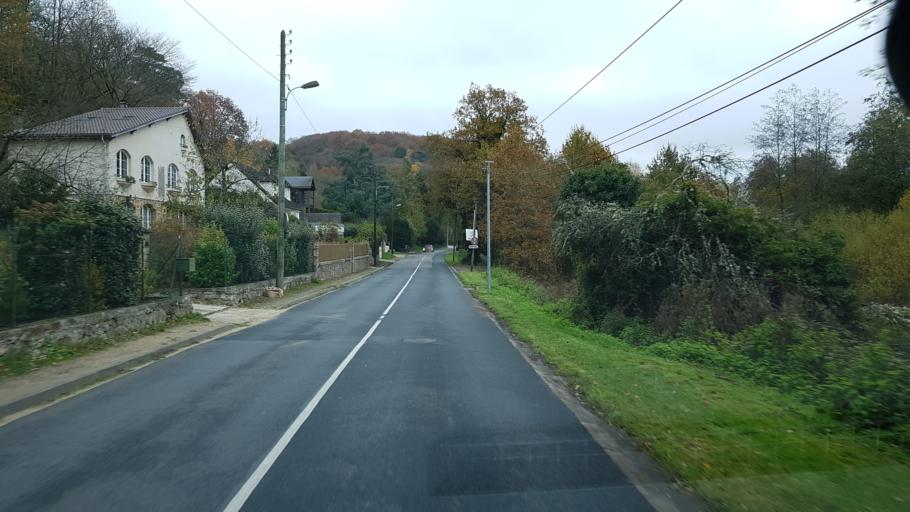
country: FR
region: Ile-de-France
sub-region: Departement des Yvelines
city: Chevreuse
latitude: 48.7130
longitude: 2.0293
